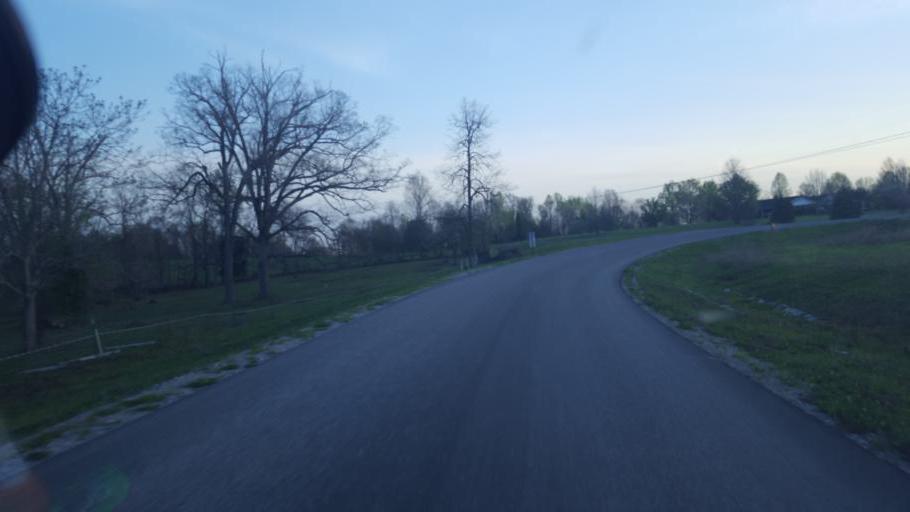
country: US
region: Kentucky
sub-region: Hart County
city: Munfordville
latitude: 37.2787
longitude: -85.9329
